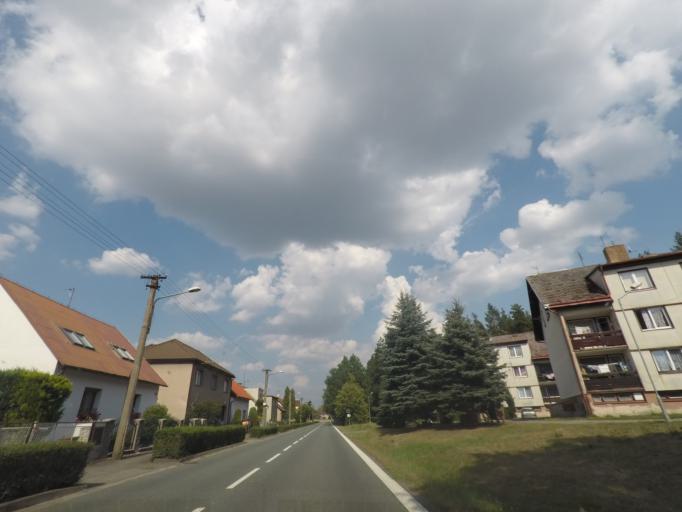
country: CZ
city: Borohradek
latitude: 50.0906
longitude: 16.0848
